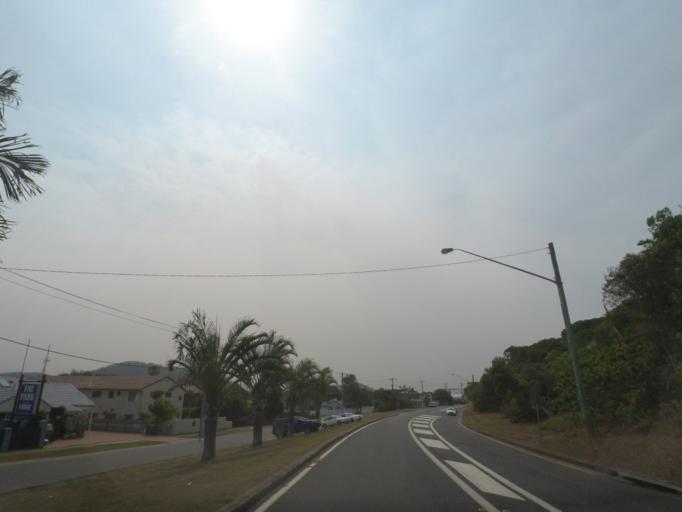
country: AU
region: New South Wales
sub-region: Tweed
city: Casuarina
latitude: -28.3341
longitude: 153.5716
